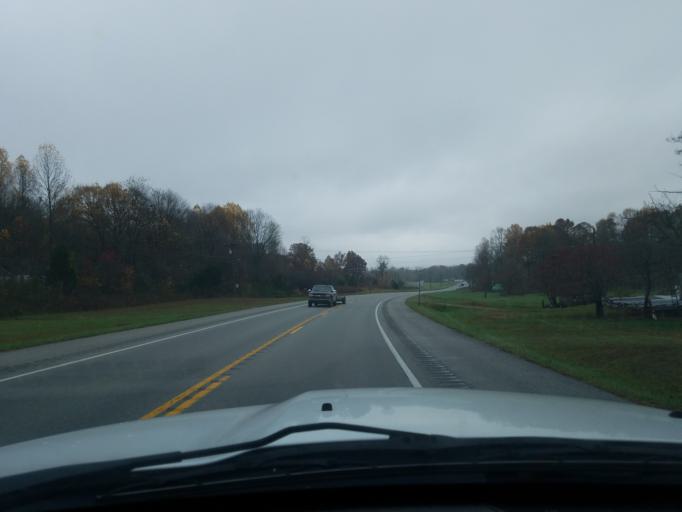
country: US
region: Kentucky
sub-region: Taylor County
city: Campbellsville
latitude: 37.3847
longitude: -85.4167
